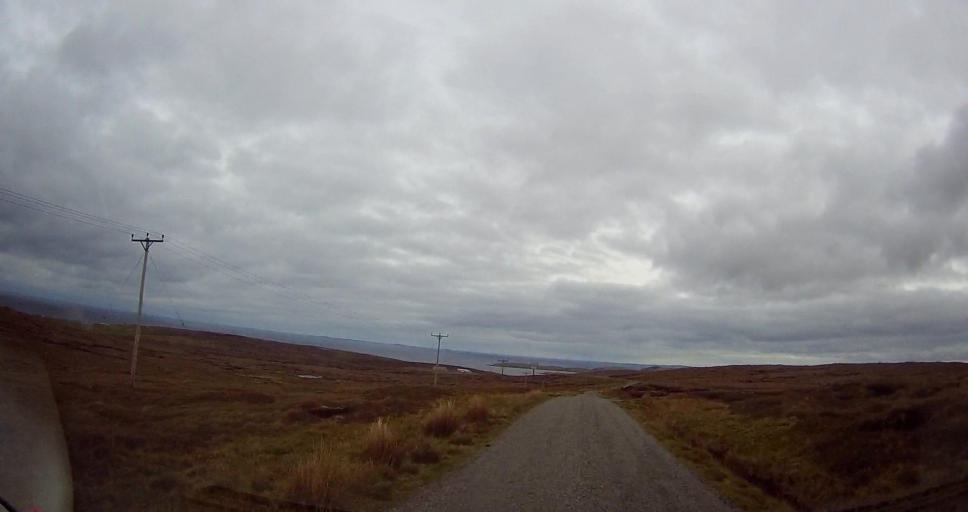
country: GB
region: Scotland
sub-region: Shetland Islands
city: Shetland
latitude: 60.5658
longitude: -1.0662
